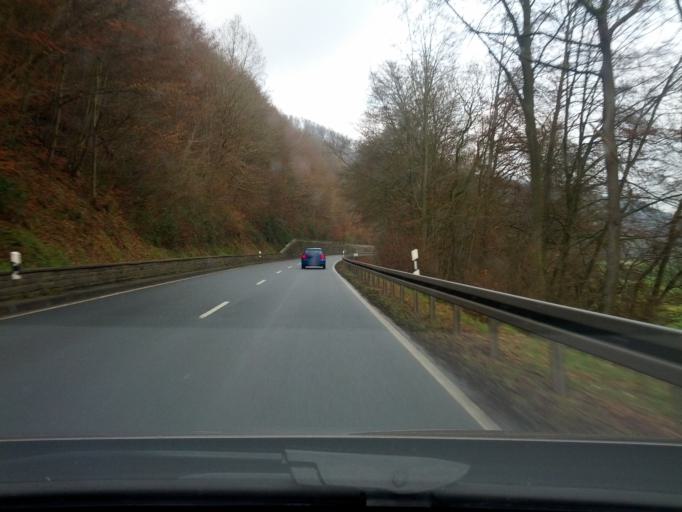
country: DE
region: Lower Saxony
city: Bodenfelde
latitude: 51.6033
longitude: 9.5381
